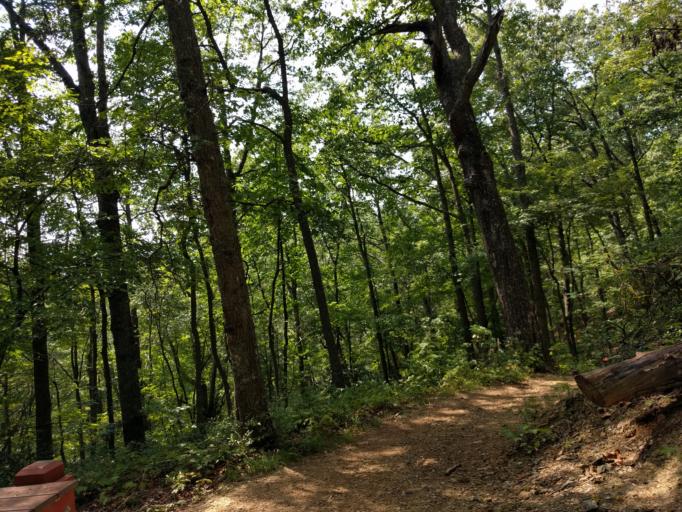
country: US
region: Virginia
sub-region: Smyth County
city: Marion
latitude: 36.8838
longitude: -81.5155
